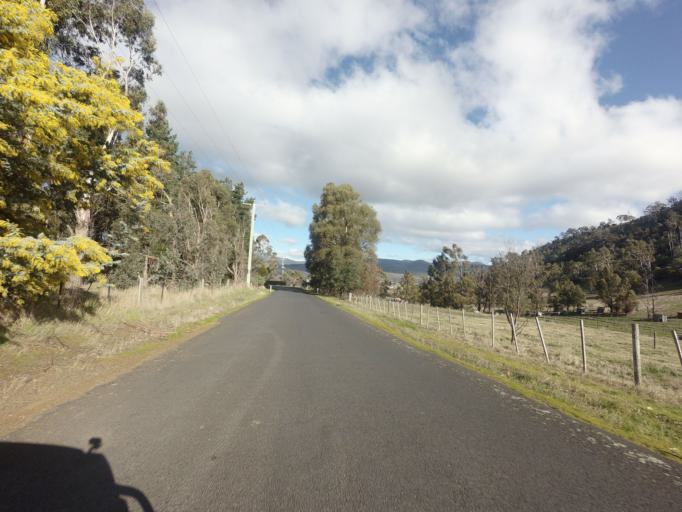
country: AU
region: Tasmania
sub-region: Derwent Valley
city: New Norfolk
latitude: -42.7502
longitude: 147.0462
